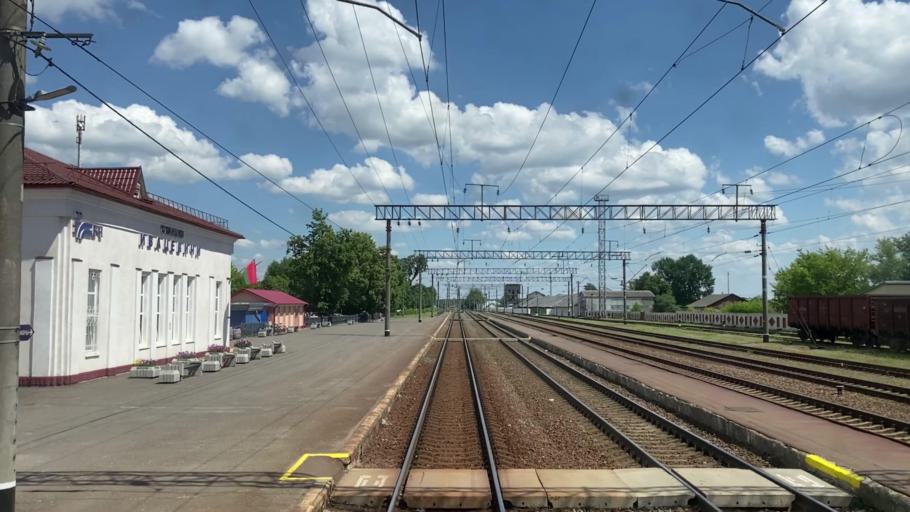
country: BY
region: Brest
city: Ivatsevichy
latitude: 52.7088
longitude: 25.3442
